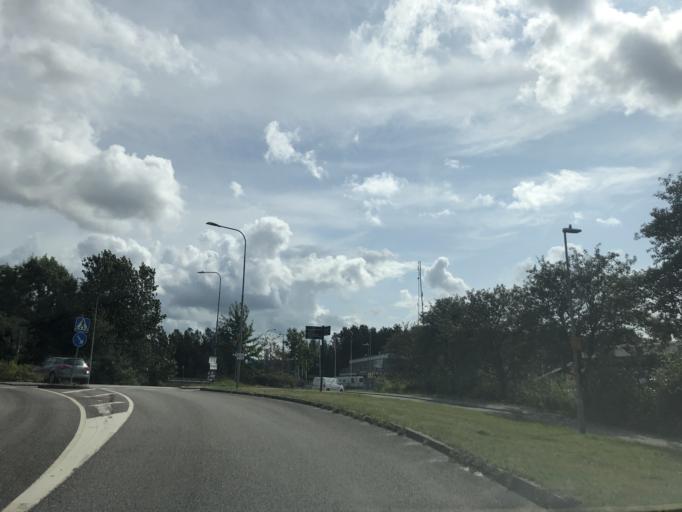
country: SE
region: Vaestra Goetaland
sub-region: Goteborg
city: Majorna
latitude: 57.7085
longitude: 11.8895
